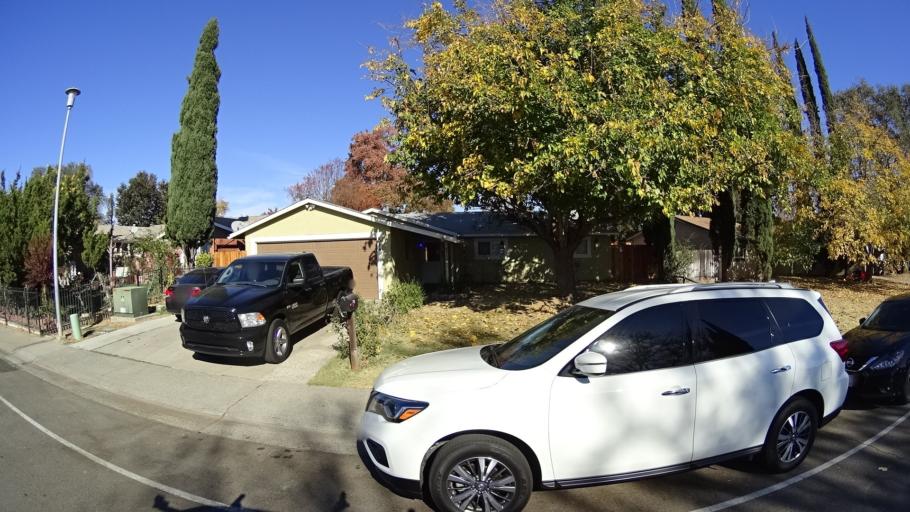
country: US
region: California
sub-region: Sacramento County
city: Antelope
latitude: 38.7170
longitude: -121.3109
